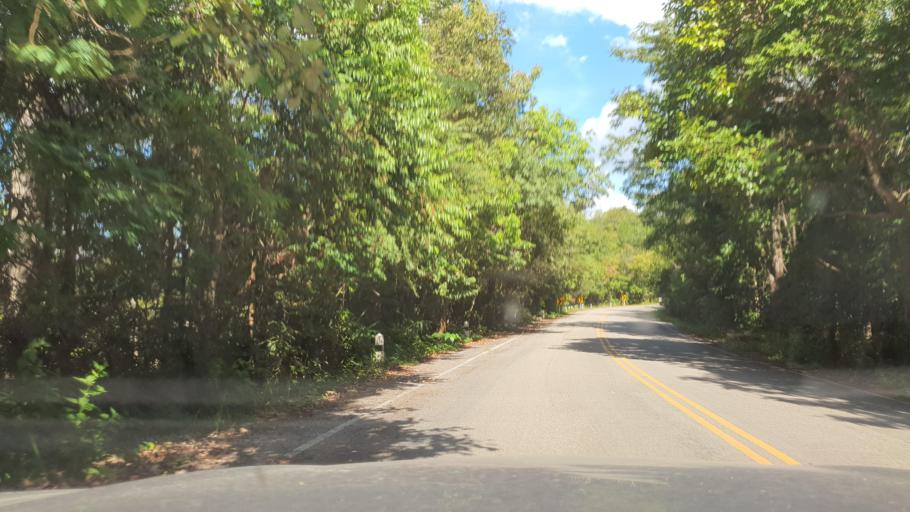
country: TH
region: Chiang Rai
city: Wiang Pa Pao
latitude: 19.3084
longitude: 99.3732
